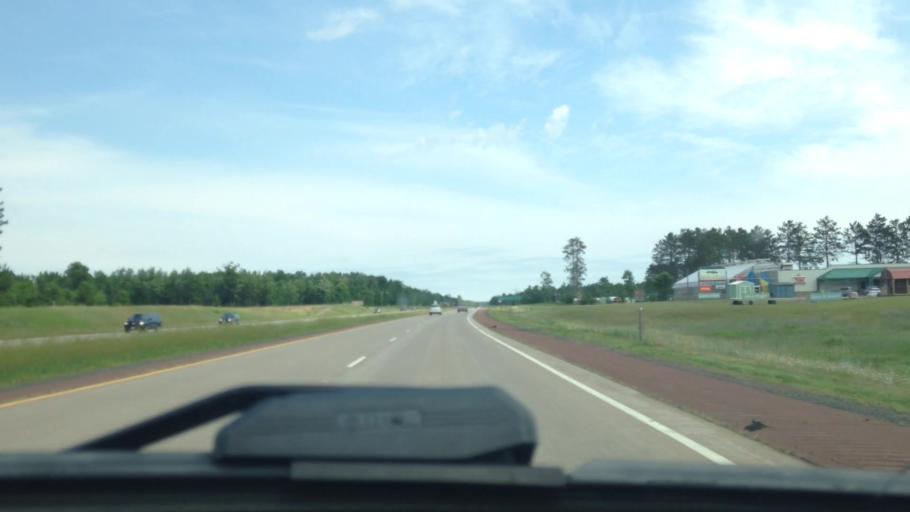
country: US
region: Wisconsin
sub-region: Douglas County
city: Lake Nebagamon
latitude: 46.3558
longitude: -91.8339
